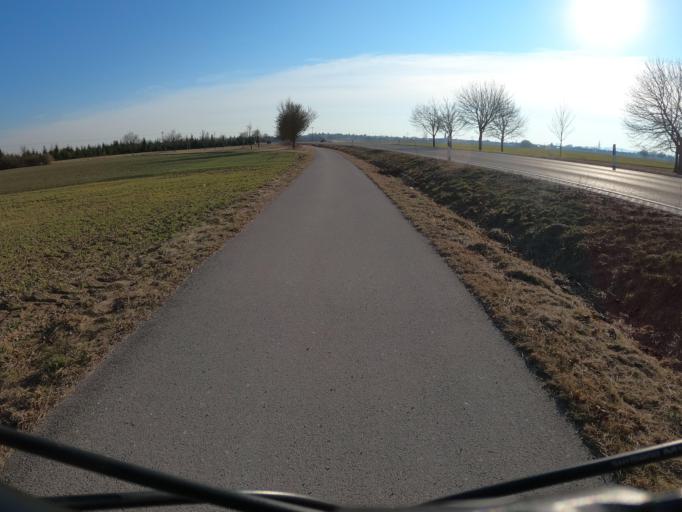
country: DE
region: Bavaria
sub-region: Swabia
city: Neu-Ulm
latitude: 48.4211
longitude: 10.0566
